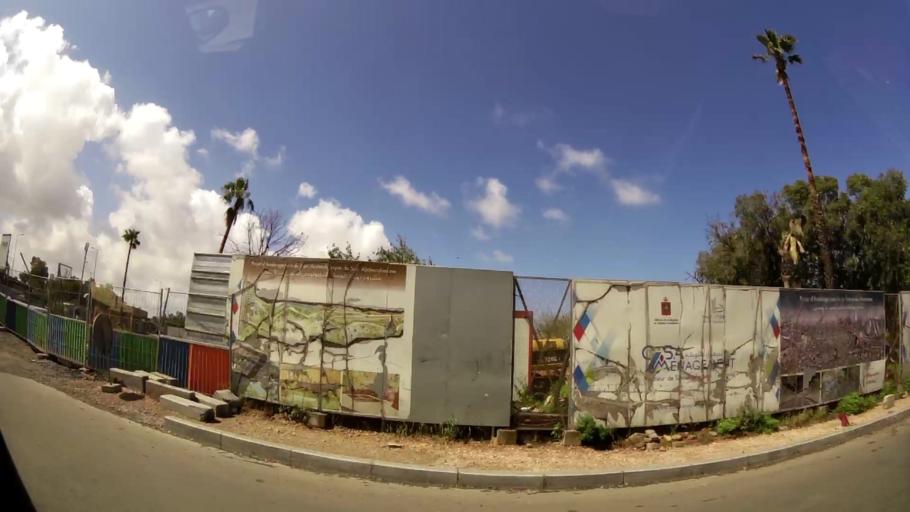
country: MA
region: Grand Casablanca
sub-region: Mediouna
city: Tit Mellil
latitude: 33.6058
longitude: -7.5279
